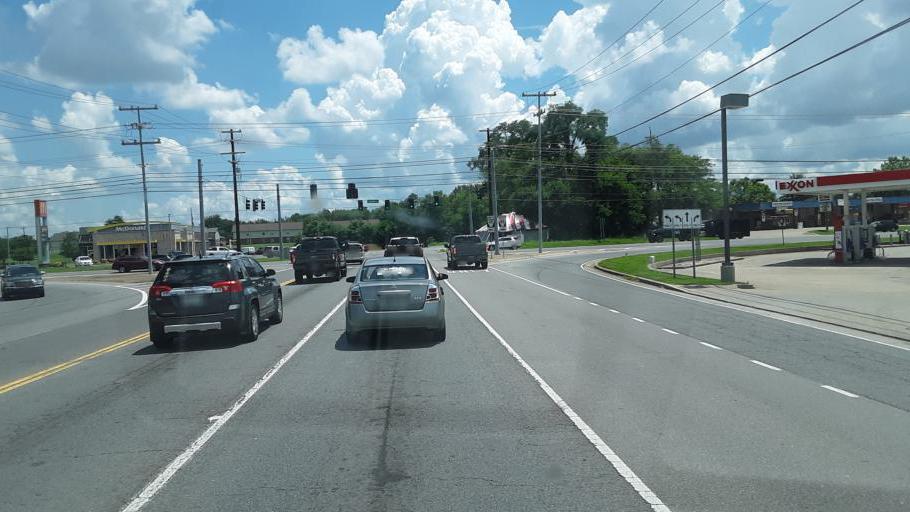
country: US
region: Tennessee
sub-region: Montgomery County
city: Clarksville
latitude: 36.6247
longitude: -87.3187
